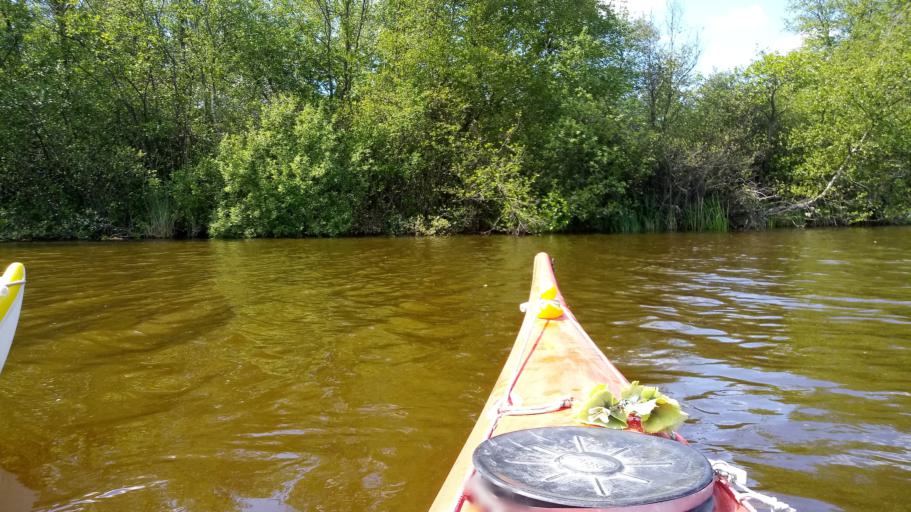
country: NL
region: South Holland
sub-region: Gemeente Nieuwkoop
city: Nieuwkoop
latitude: 52.1506
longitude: 4.8297
